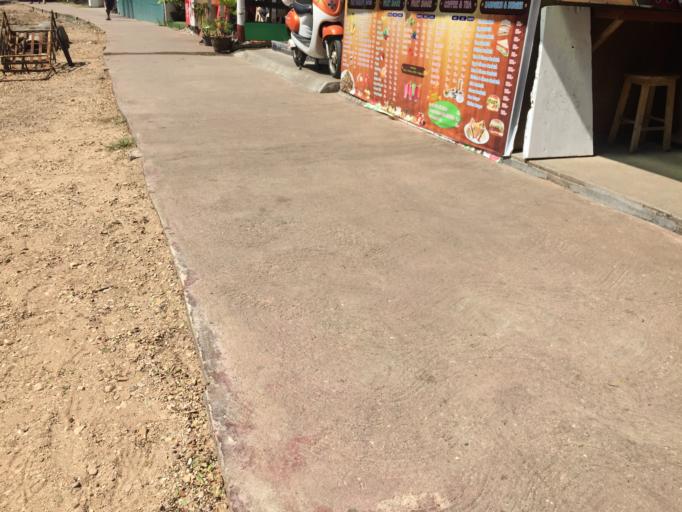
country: TH
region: Phangnga
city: Ban Ao Nang
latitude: 8.0120
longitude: 98.8426
